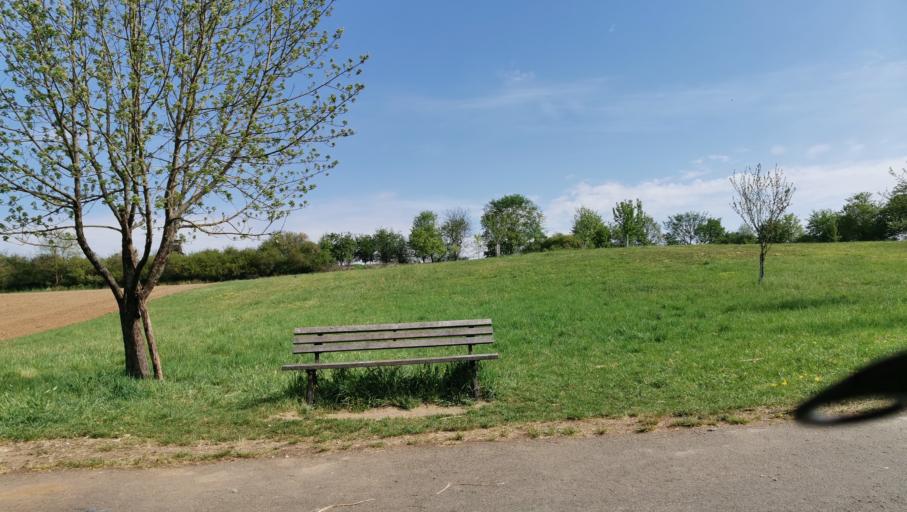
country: DE
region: Hesse
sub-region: Regierungsbezirk Darmstadt
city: Karben
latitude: 50.2435
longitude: 8.7364
